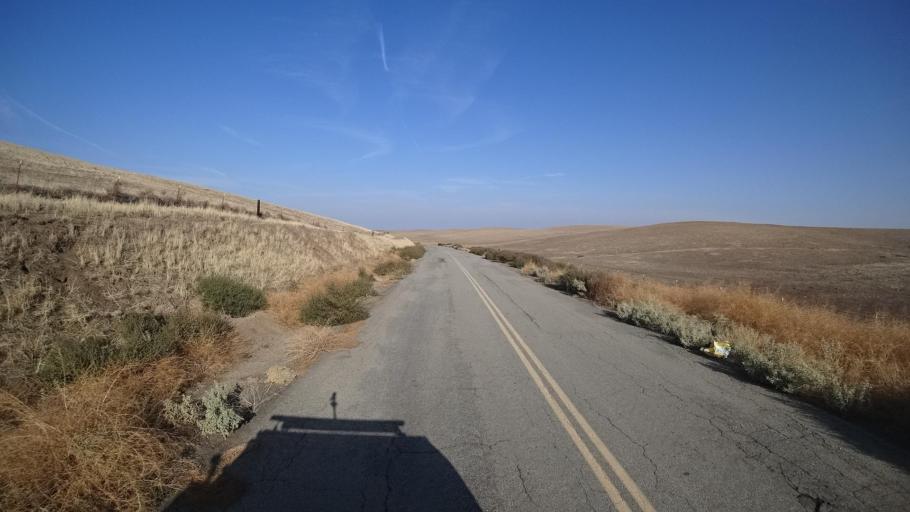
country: US
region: California
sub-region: Tulare County
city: Richgrove
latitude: 35.6307
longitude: -119.0329
